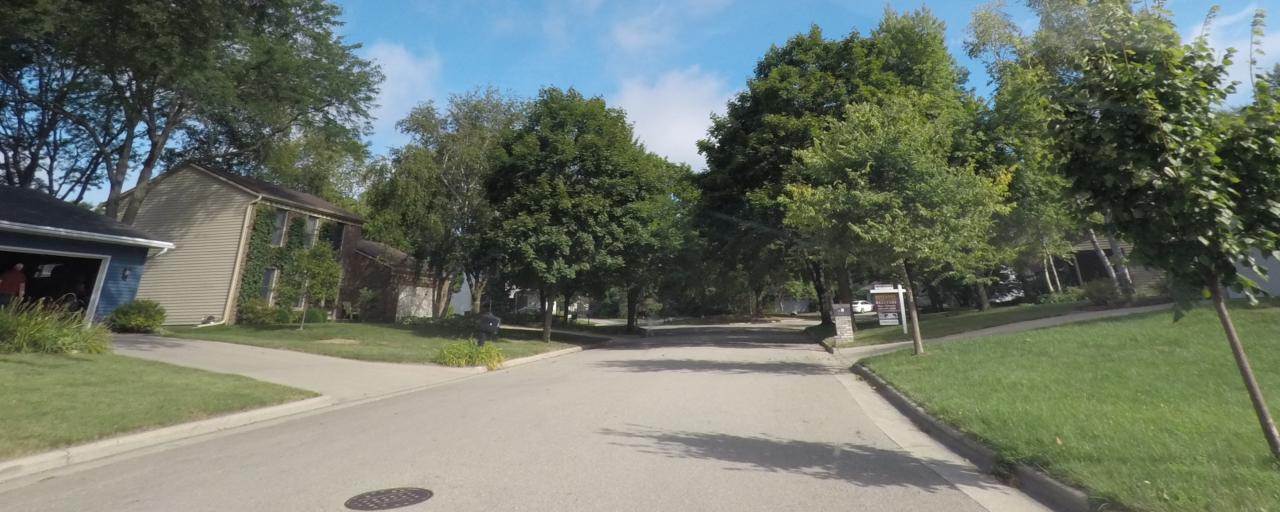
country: US
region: Wisconsin
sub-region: Dane County
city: Middleton
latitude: 43.0791
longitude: -89.5047
